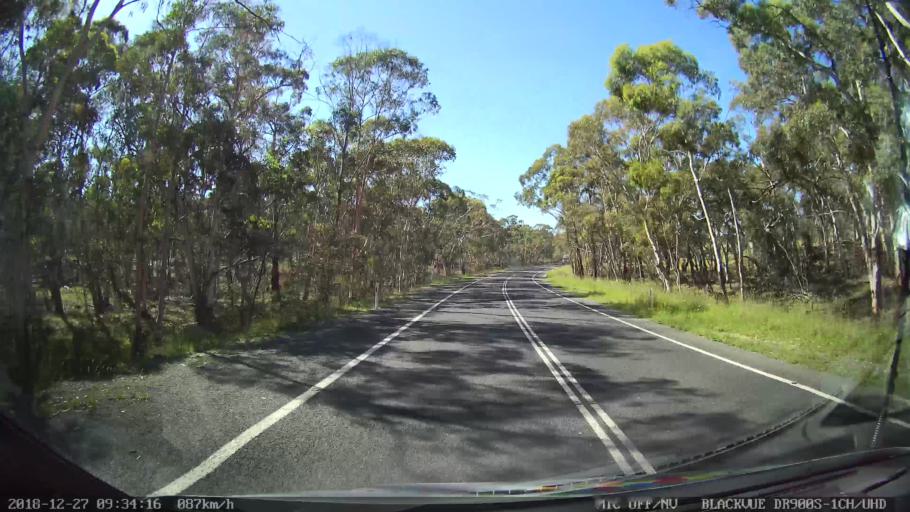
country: AU
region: New South Wales
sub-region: Lithgow
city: Portland
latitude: -33.2239
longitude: 150.0273
